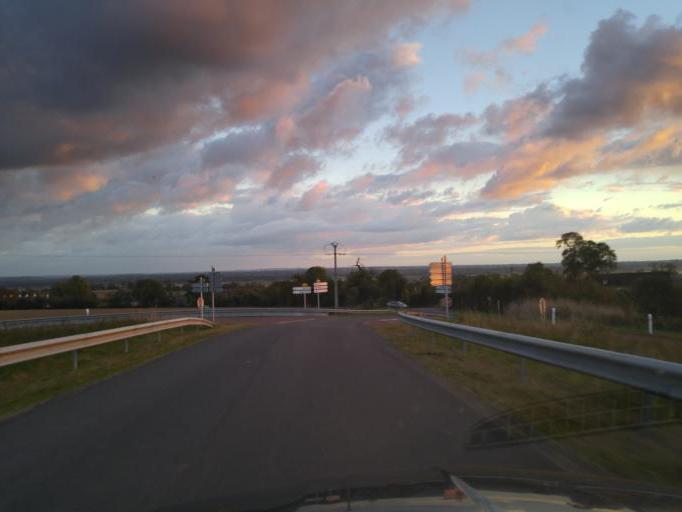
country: FR
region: Lower Normandy
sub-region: Departement du Calvados
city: Grandcamp-Maisy
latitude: 49.3408
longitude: -0.9803
